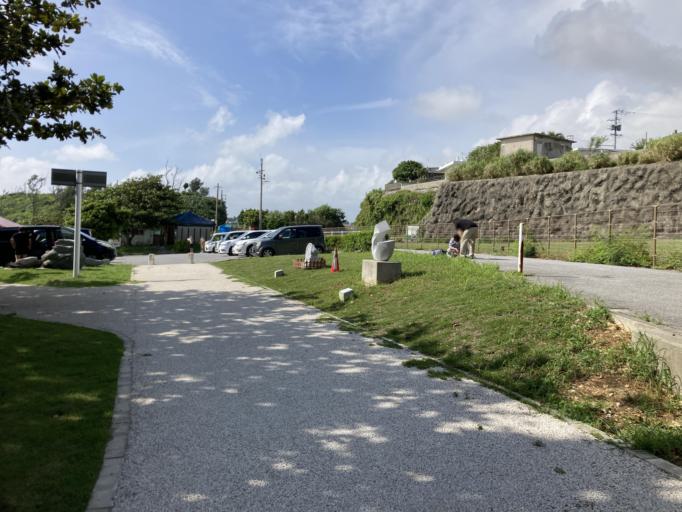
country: JP
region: Okinawa
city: Itoman
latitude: 26.0903
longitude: 127.7094
